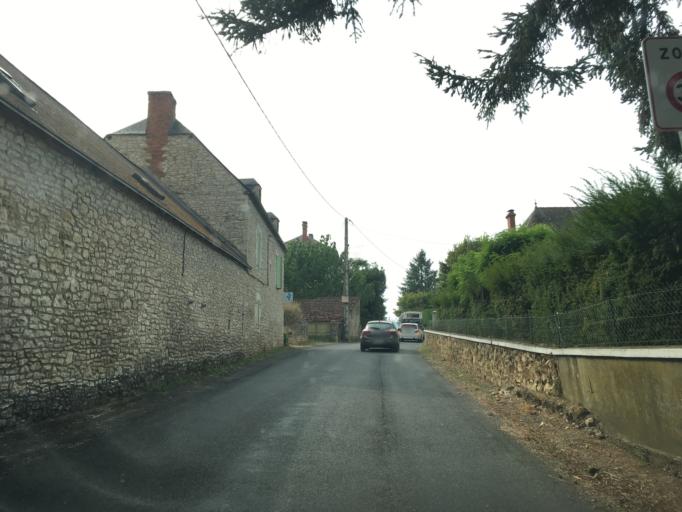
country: FR
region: Midi-Pyrenees
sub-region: Departement du Lot
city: Souillac
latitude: 44.8541
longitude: 1.5155
